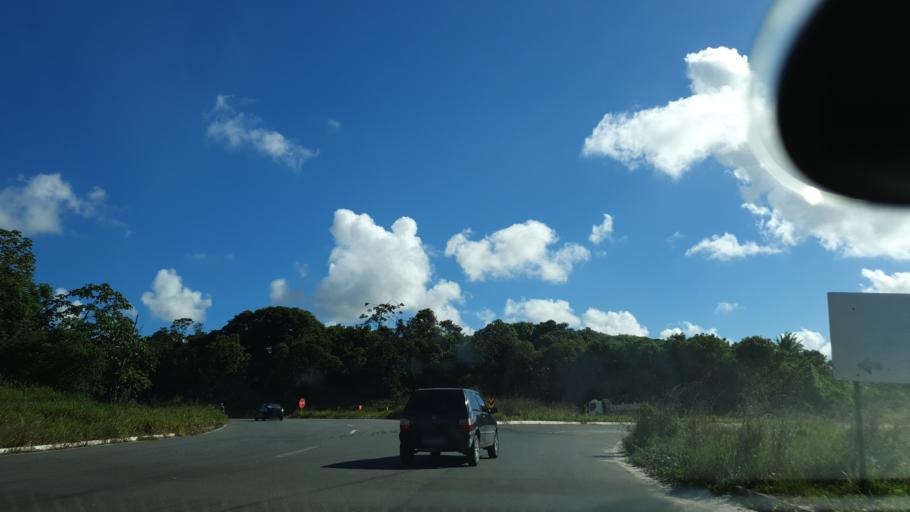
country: BR
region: Bahia
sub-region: Camacari
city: Camacari
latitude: -12.6796
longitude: -38.2833
